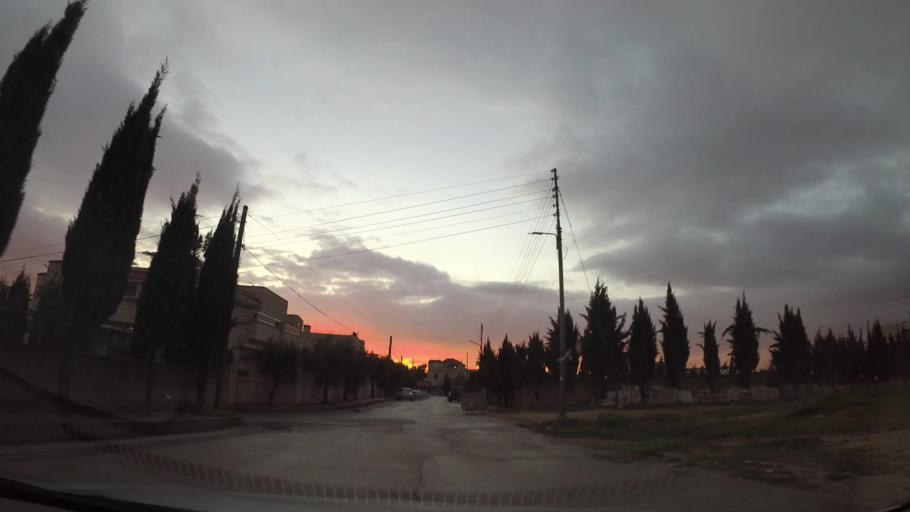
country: JO
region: Amman
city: Al Jubayhah
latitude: 32.0336
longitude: 35.8187
